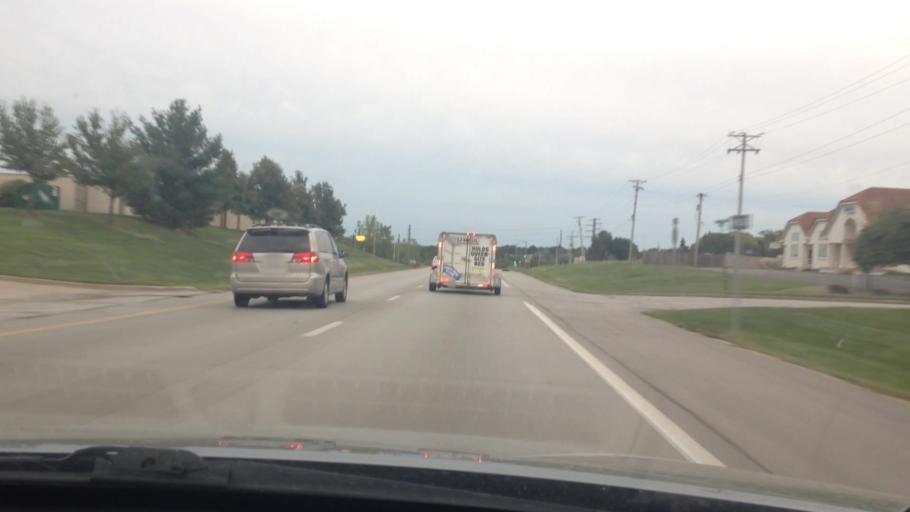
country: US
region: Missouri
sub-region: Jackson County
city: Raytown
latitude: 38.9736
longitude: -94.4441
